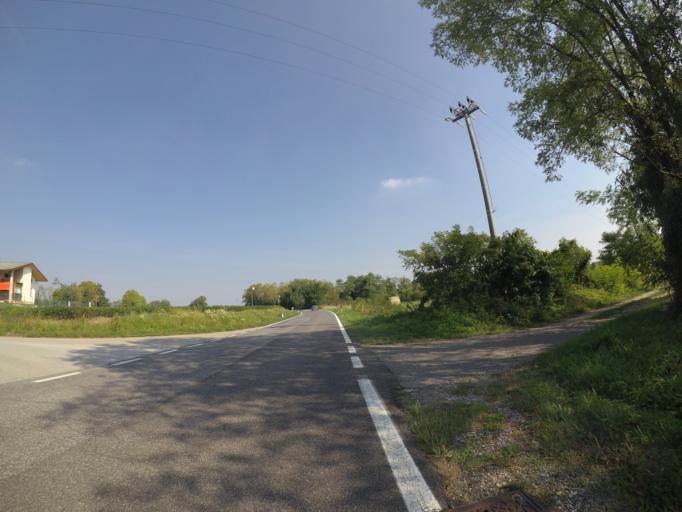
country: IT
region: Friuli Venezia Giulia
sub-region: Provincia di Udine
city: Basiliano-Vissandone
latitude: 46.0142
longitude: 13.0942
